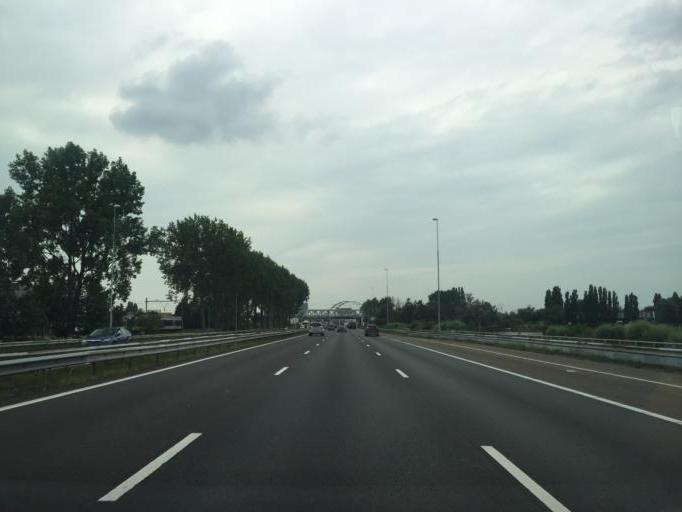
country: NL
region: South Holland
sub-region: Gemeente Pijnacker-Nootdorp
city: Pijnacker
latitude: 52.0524
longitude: 4.4163
